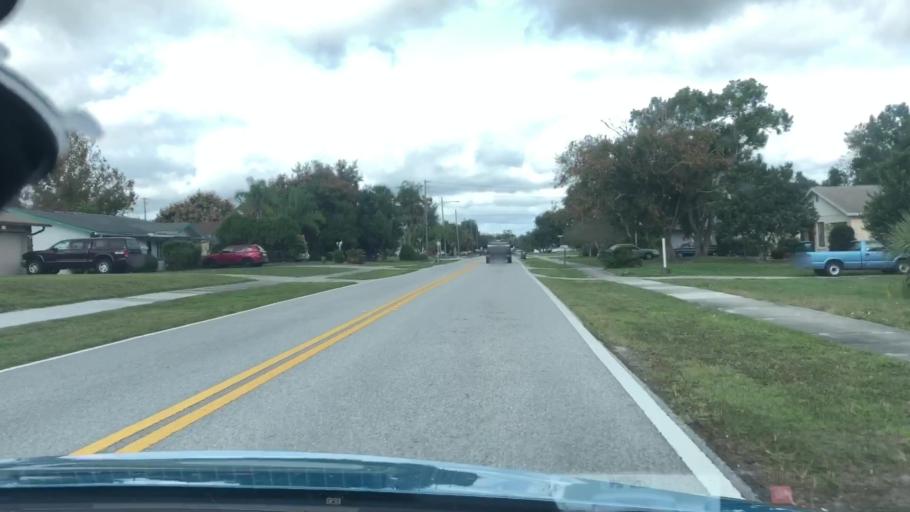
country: US
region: Florida
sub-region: Volusia County
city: Deltona
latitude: 28.8872
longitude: -81.2439
